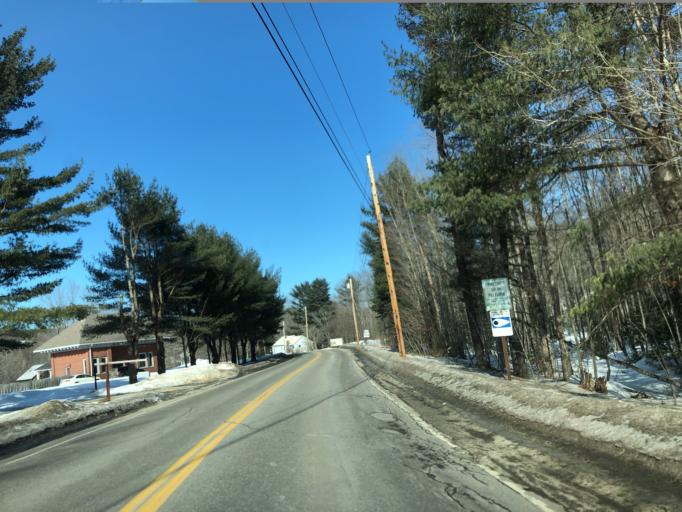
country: US
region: Maine
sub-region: Oxford County
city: Hebron
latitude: 44.1687
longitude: -70.3655
